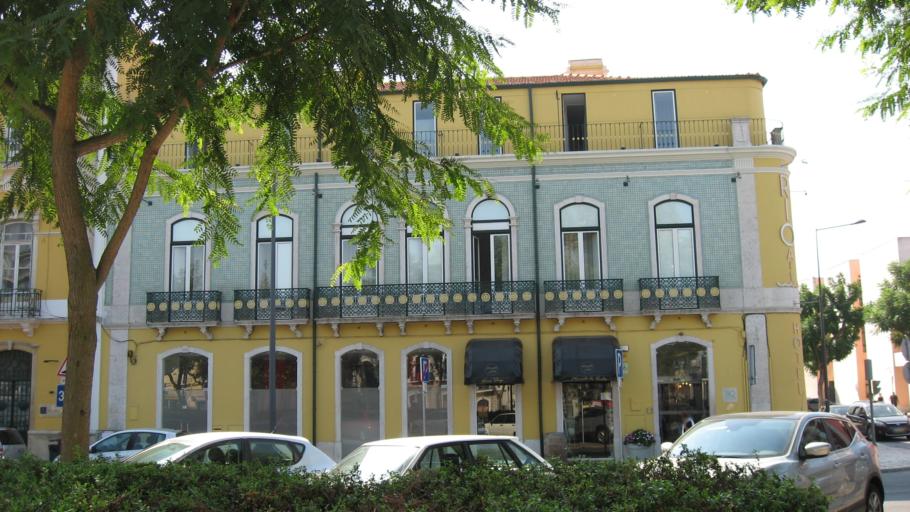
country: PT
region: Setubal
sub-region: Setubal
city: Setubal
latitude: 38.5230
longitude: -8.8917
